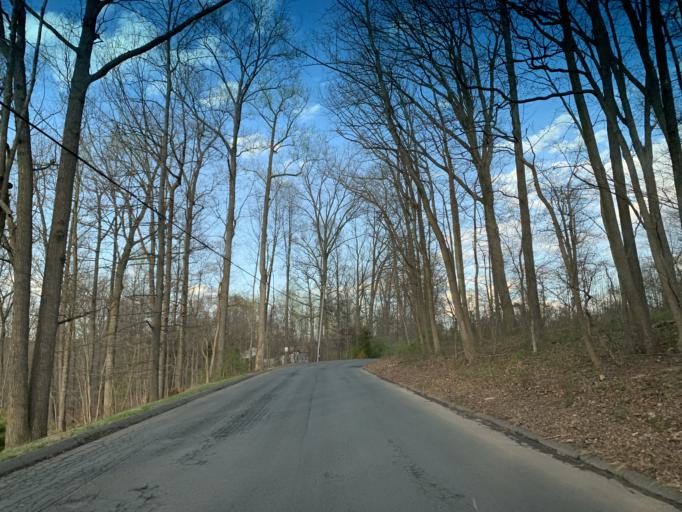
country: US
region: Maryland
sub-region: Harford County
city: South Bel Air
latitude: 39.6107
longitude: -76.2937
